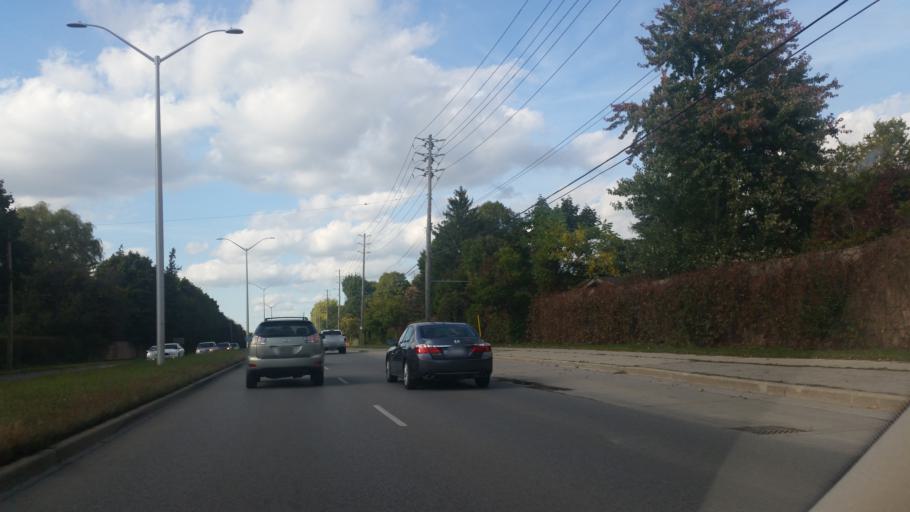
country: CA
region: Ontario
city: London
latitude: 42.9969
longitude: -81.2994
